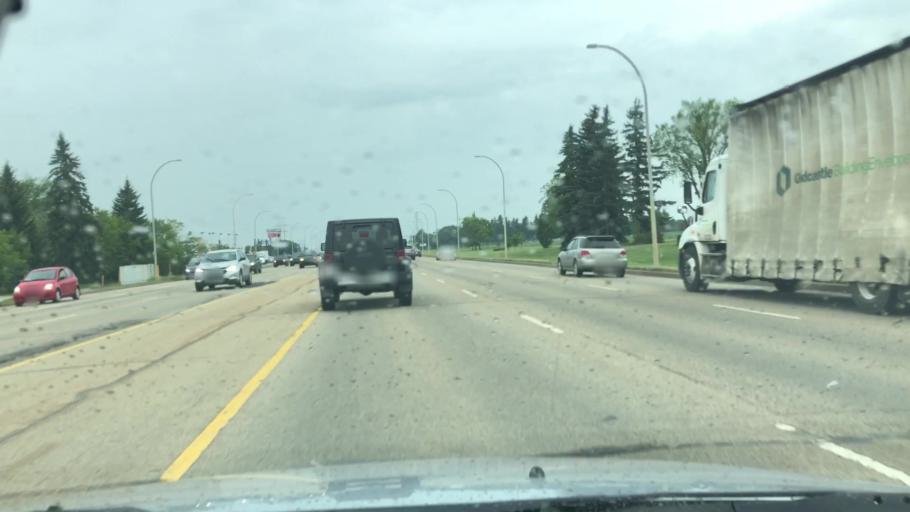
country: CA
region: Alberta
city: St. Albert
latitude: 53.6083
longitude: -113.5854
